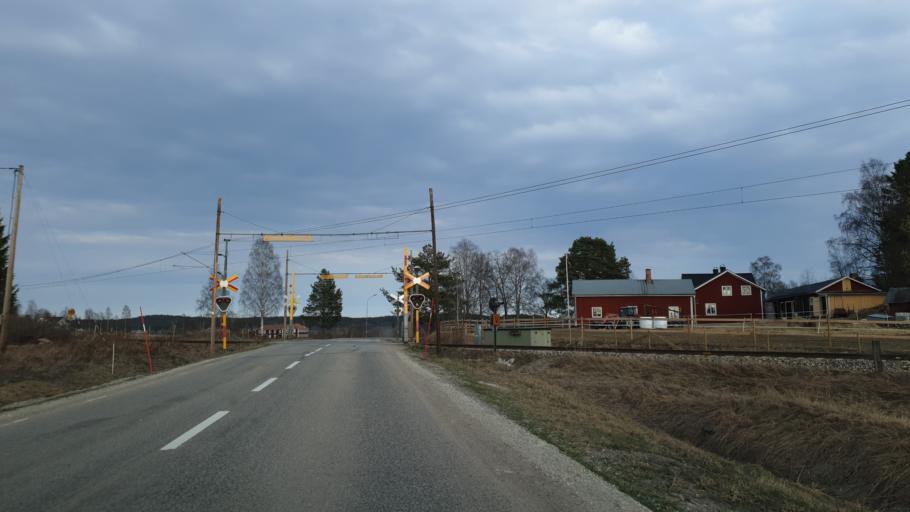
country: SE
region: Gaevleborg
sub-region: Nordanstigs Kommun
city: Bergsjoe
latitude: 61.9773
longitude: 17.2464
